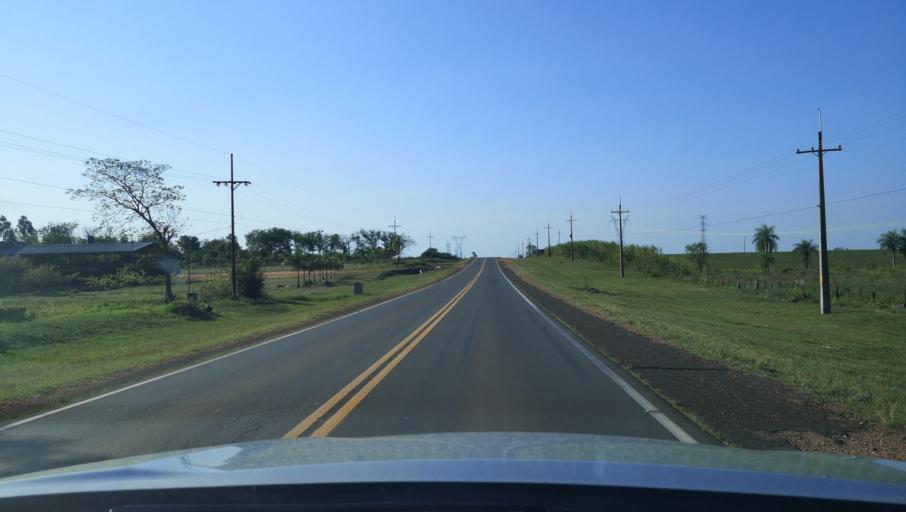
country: PY
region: Misiones
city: Santa Maria
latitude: -26.7982
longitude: -57.0224
